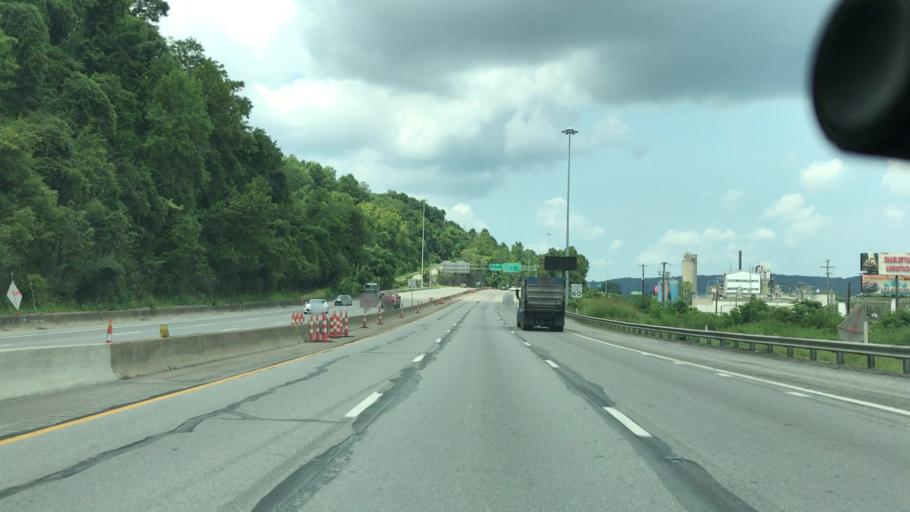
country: US
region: West Virginia
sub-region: Kanawha County
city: Charleston
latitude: 38.3571
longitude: -81.6569
